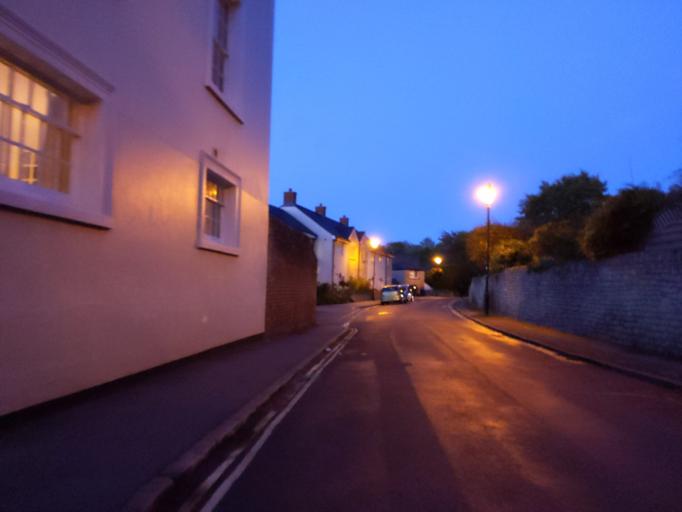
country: GB
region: England
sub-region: Oxfordshire
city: Oxford
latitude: 51.7317
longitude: -1.2354
